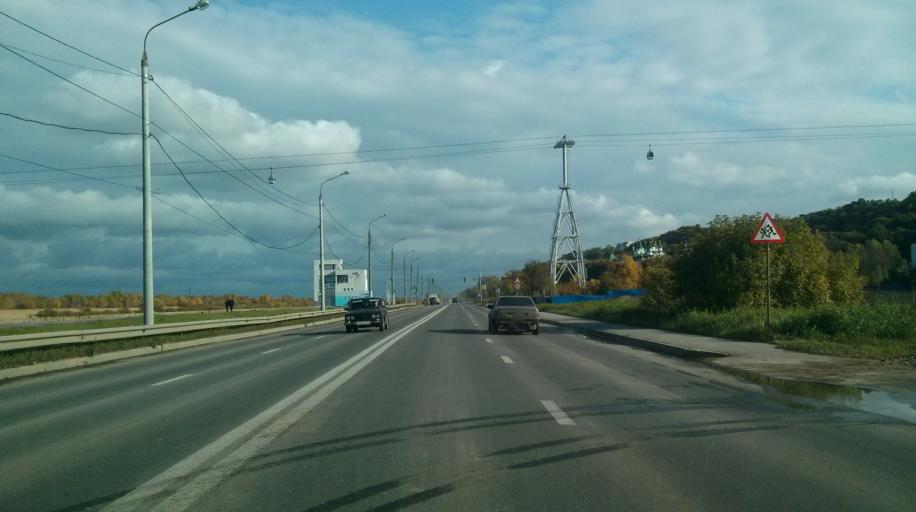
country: RU
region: Nizjnij Novgorod
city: Nizhniy Novgorod
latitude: 56.3280
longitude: 44.0379
